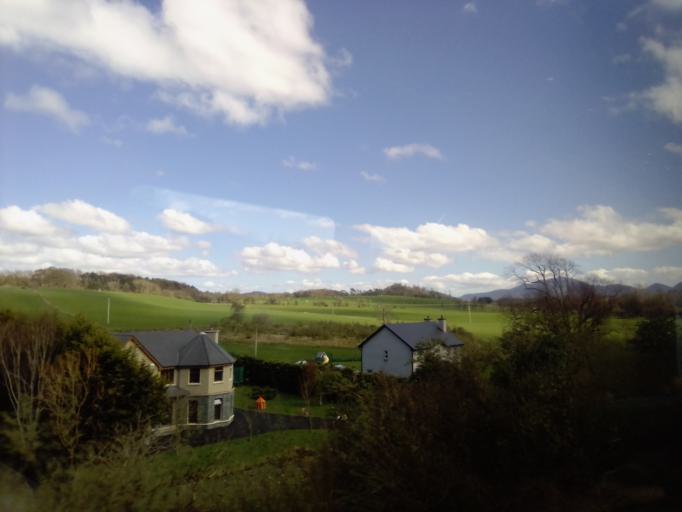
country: IE
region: Munster
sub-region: Ciarrai
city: Cill Airne
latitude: 52.0731
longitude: -9.5079
